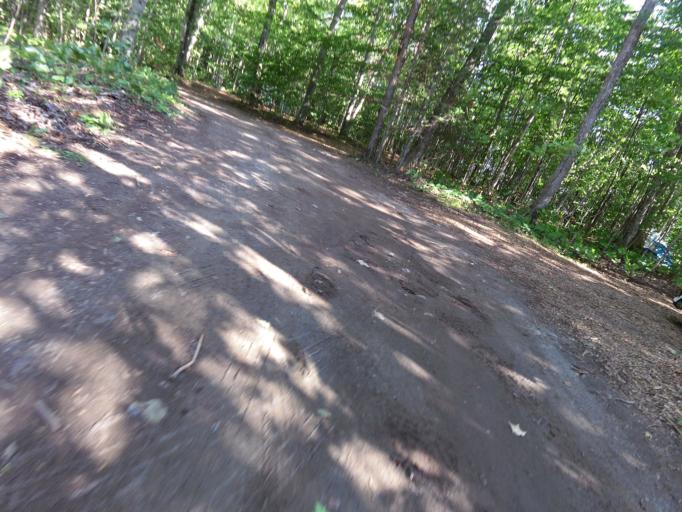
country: CA
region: Ontario
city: Tobermory
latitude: 45.2283
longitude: -81.6460
